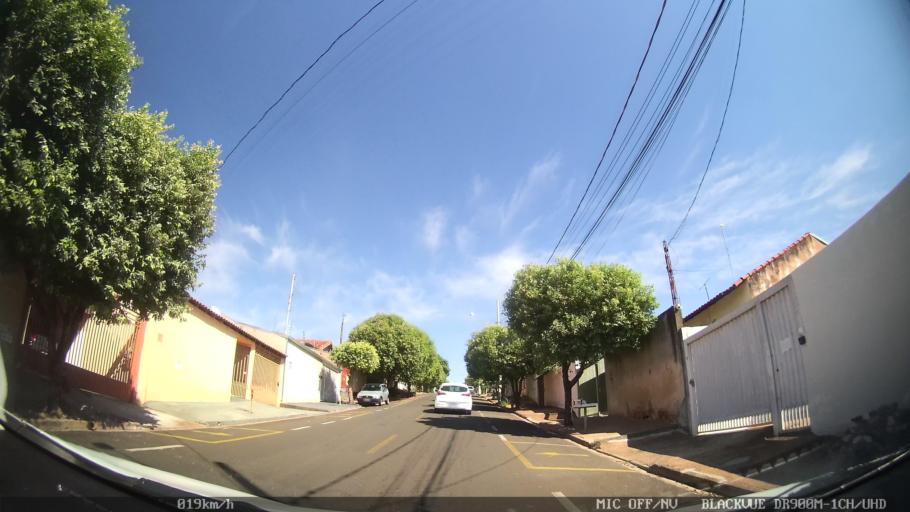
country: BR
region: Sao Paulo
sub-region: Sao Jose Do Rio Preto
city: Sao Jose do Rio Preto
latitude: -20.7745
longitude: -49.4017
